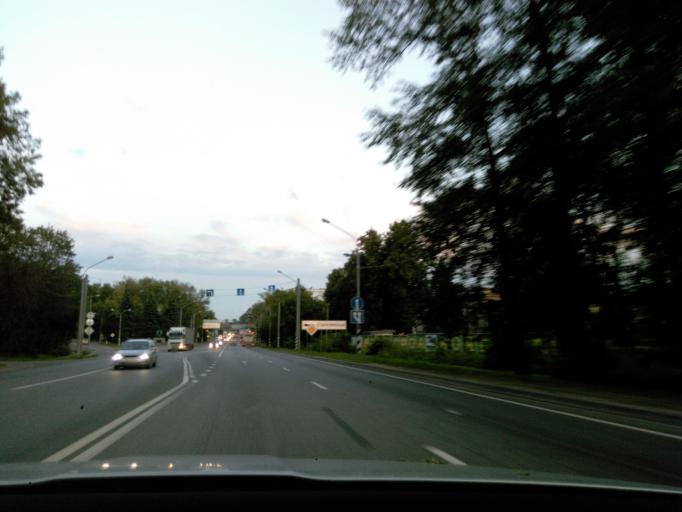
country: RU
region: Moskovskaya
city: Klin
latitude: 56.3412
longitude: 36.7134
